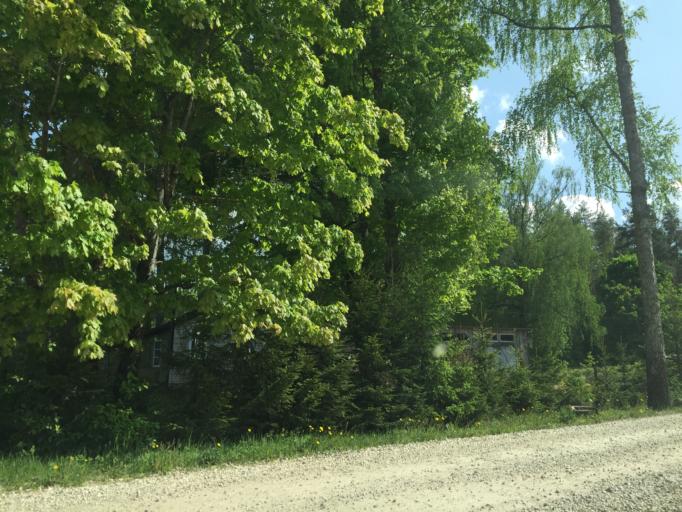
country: LV
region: Baldone
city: Baldone
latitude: 56.8062
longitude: 24.4253
